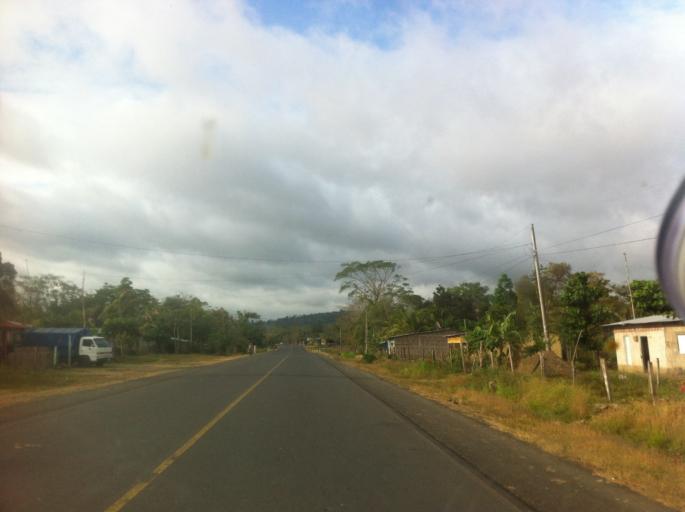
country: NI
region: Rio San Juan
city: San Carlos
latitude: 11.2360
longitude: -84.6900
